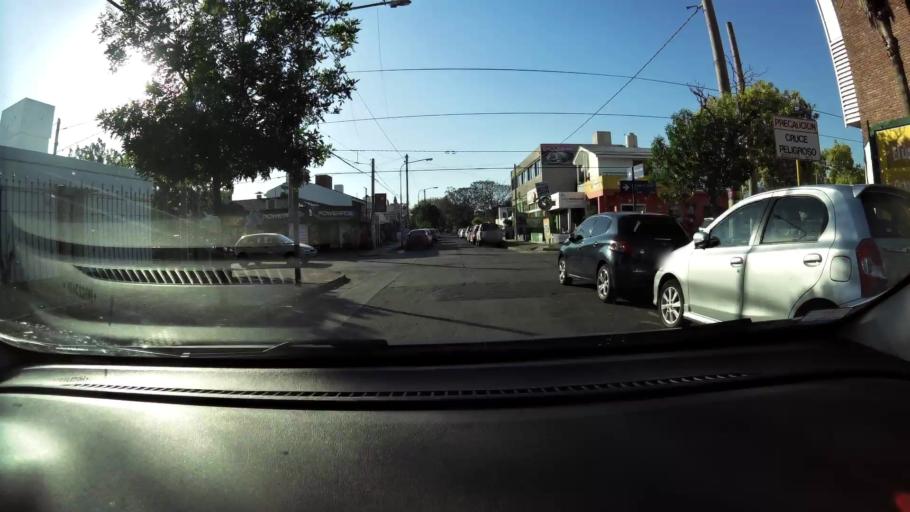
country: AR
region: Cordoba
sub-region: Departamento de Capital
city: Cordoba
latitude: -31.3829
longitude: -64.2312
